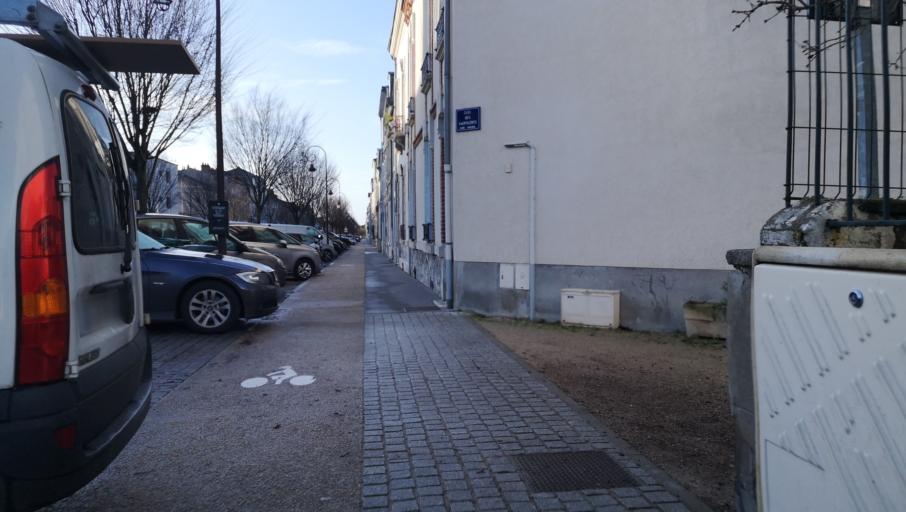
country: FR
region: Centre
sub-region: Departement du Loiret
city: Orleans
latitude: 47.9124
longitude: 1.8942
